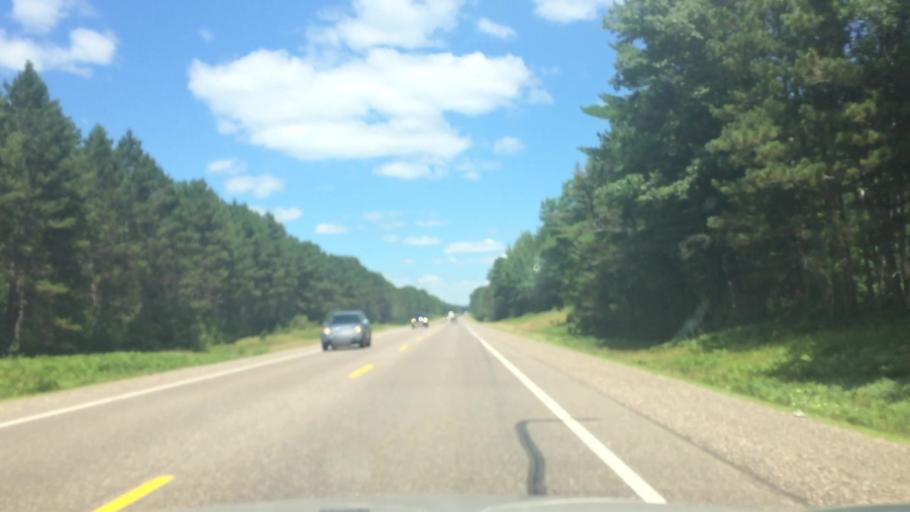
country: US
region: Wisconsin
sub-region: Vilas County
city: Lac du Flambeau
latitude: 45.9627
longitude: -89.7001
